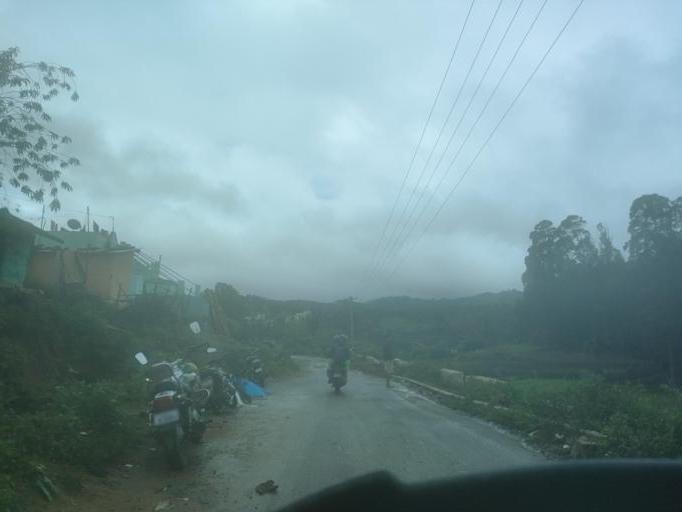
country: IN
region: Tamil Nadu
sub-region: Dindigul
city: Kodaikanal
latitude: 10.2263
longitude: 77.3525
